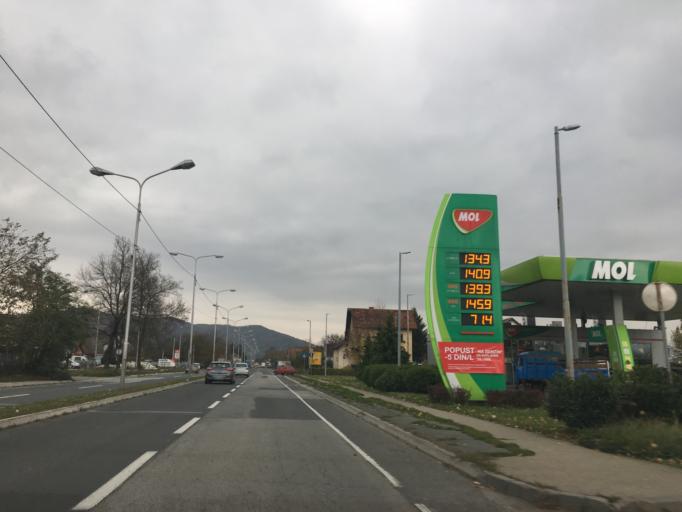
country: RS
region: Central Serbia
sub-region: Raski Okrug
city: Kraljevo
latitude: 43.7258
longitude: 20.7191
